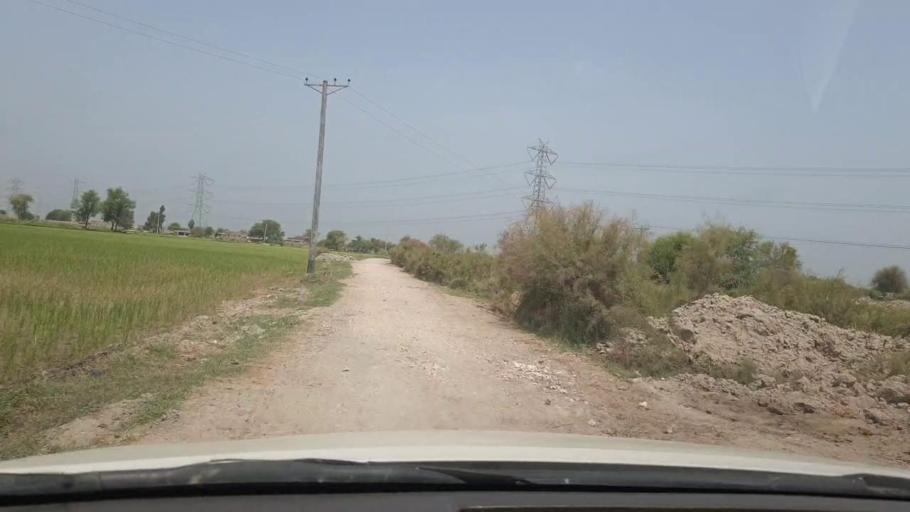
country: PK
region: Sindh
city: Shikarpur
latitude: 28.0268
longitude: 68.6467
